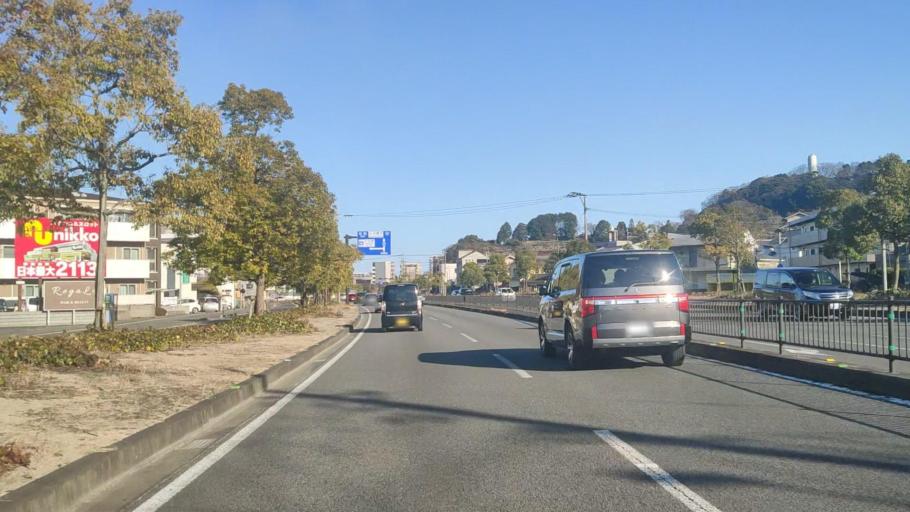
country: JP
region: Oita
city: Oita
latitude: 33.2265
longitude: 131.5984
